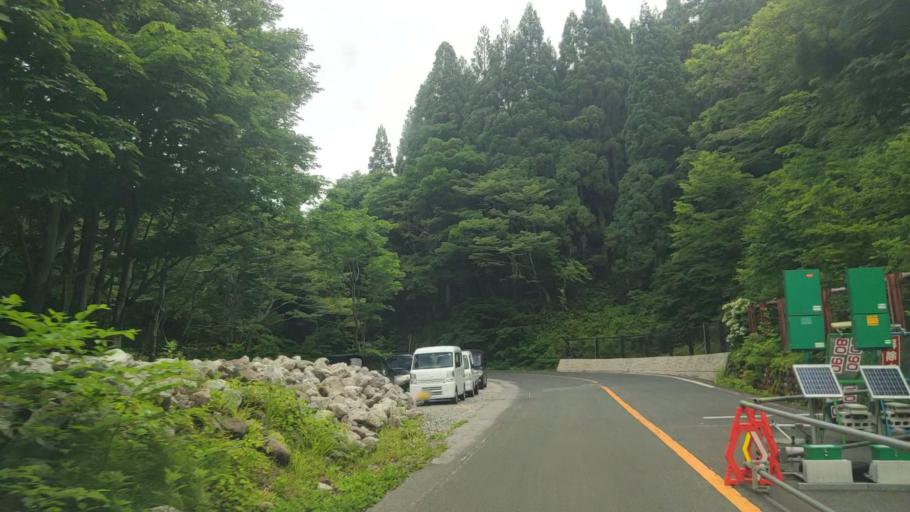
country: JP
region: Tottori
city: Yonago
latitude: 35.3521
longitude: 133.5482
